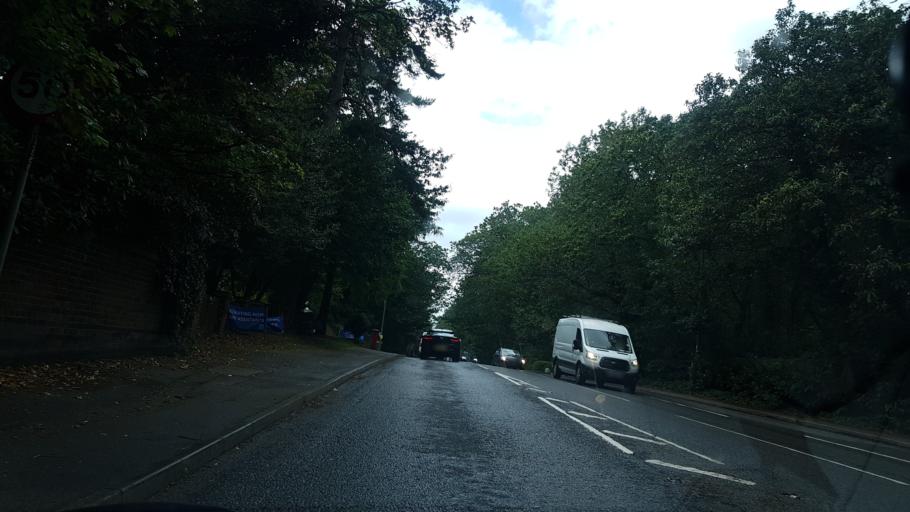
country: GB
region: England
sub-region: Surrey
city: Cobham
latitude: 51.3356
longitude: -0.4351
